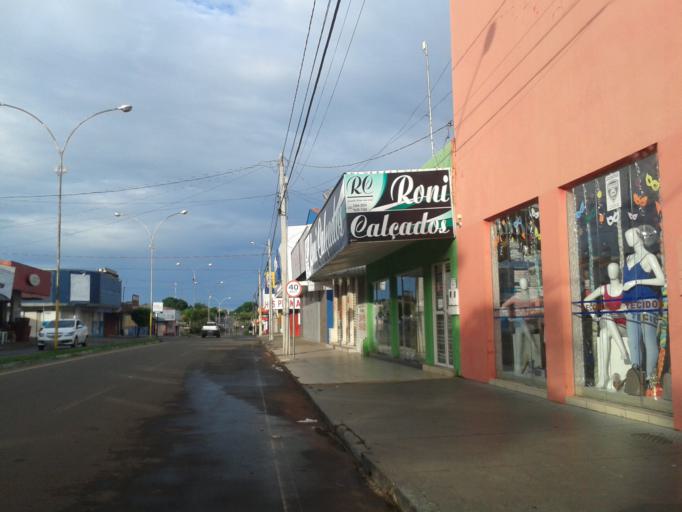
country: BR
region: Goias
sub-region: Sao Miguel Do Araguaia
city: Sao Miguel do Araguaia
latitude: -13.2725
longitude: -50.1634
